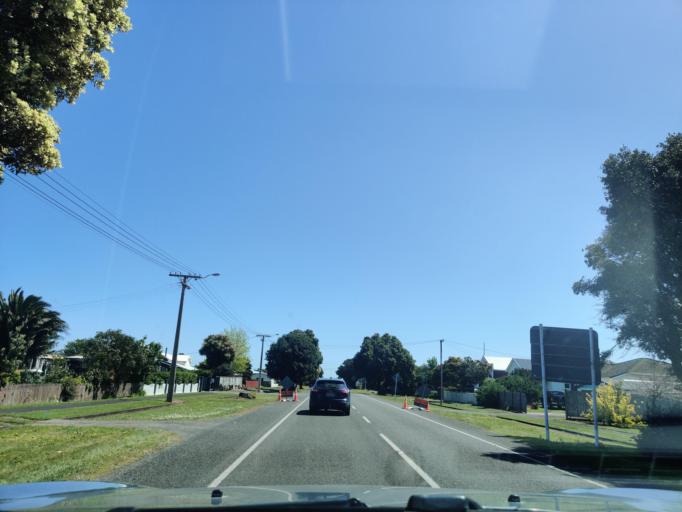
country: NZ
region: Taranaki
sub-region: South Taranaki District
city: Hawera
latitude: -39.5506
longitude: 174.1215
